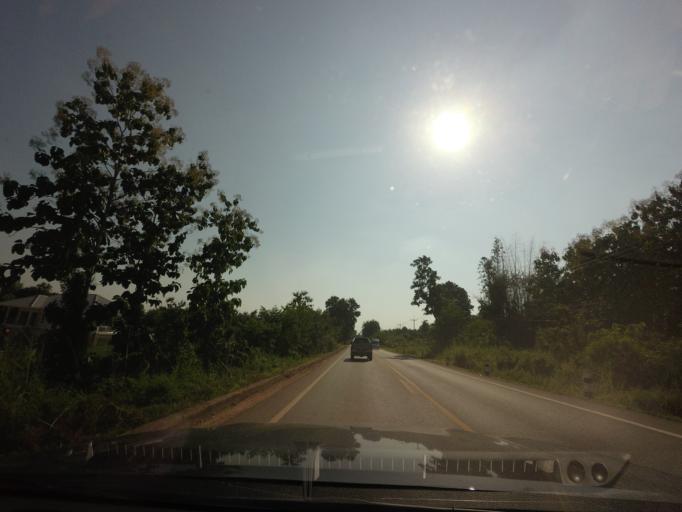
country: TH
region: Nan
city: Nan
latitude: 18.8120
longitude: 100.8037
